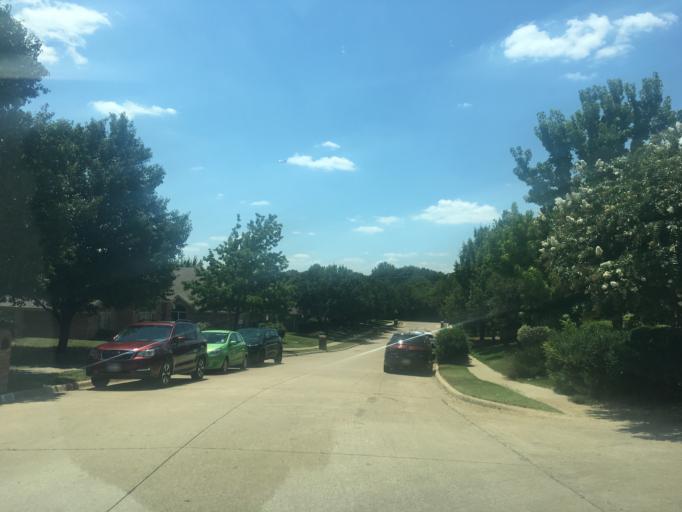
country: US
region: Texas
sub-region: Denton County
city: Lewisville
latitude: 33.0215
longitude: -96.9991
